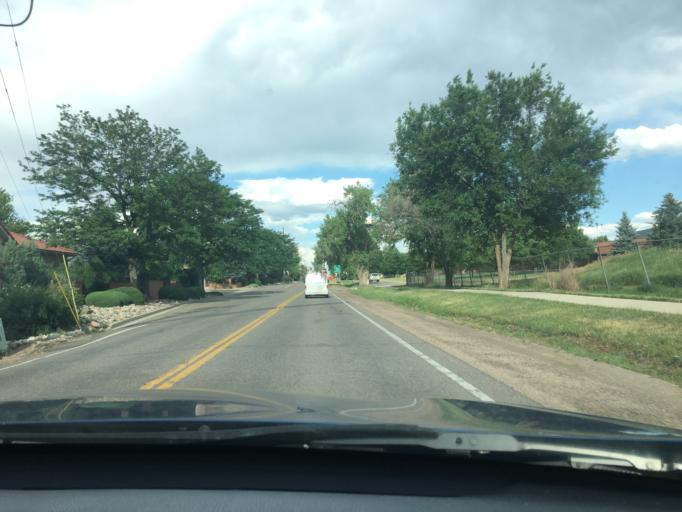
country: US
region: Colorado
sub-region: Jefferson County
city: Applewood
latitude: 39.7618
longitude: -105.1505
